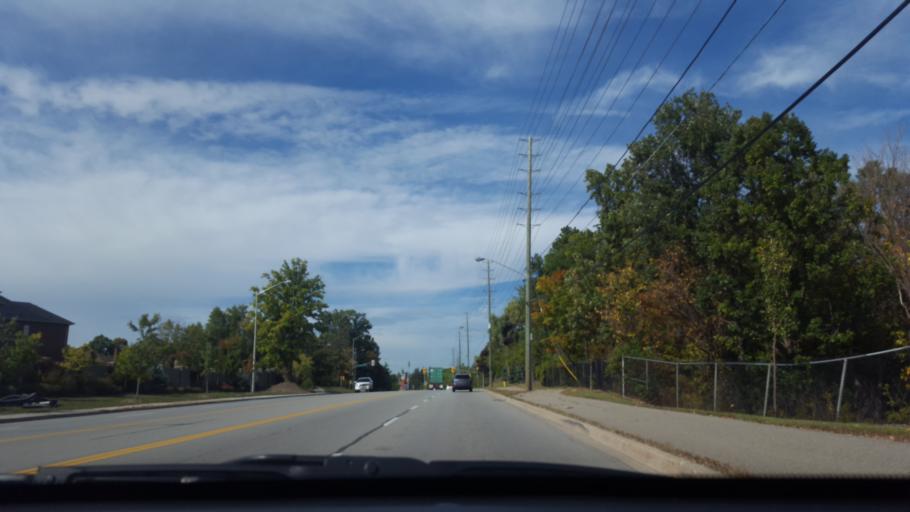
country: CA
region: Ontario
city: Vaughan
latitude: 43.8058
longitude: -79.5862
